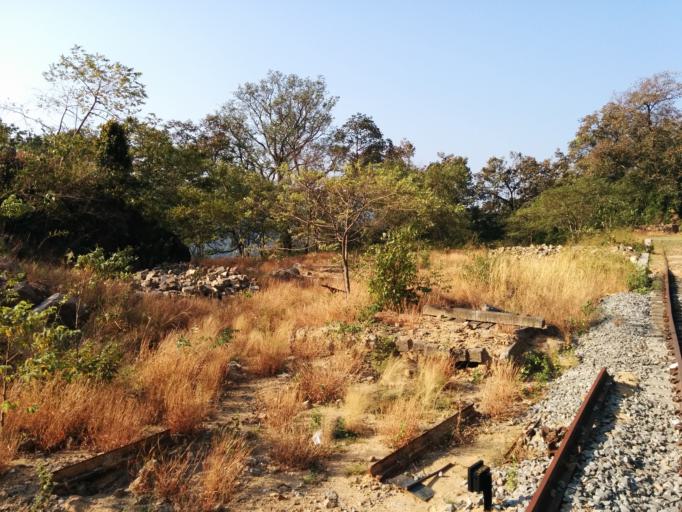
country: IN
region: Goa
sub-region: South Goa
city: Sanguem
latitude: 15.3203
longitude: 74.3035
